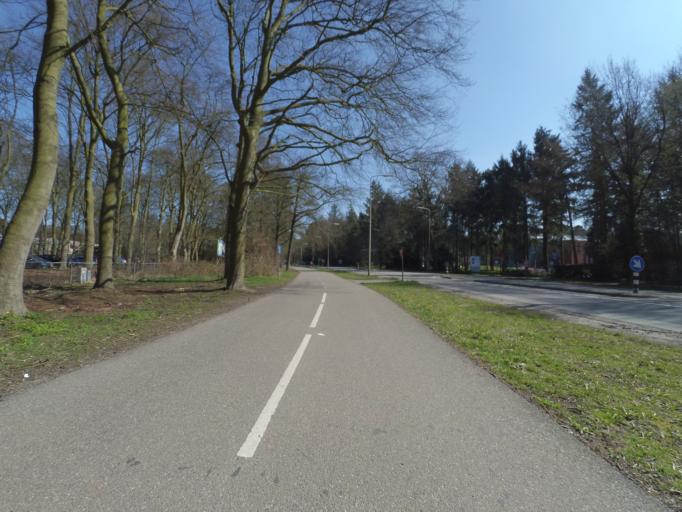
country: NL
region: Utrecht
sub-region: Gemeente Utrechtse Heuvelrug
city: Doorn
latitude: 52.0359
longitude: 5.3244
